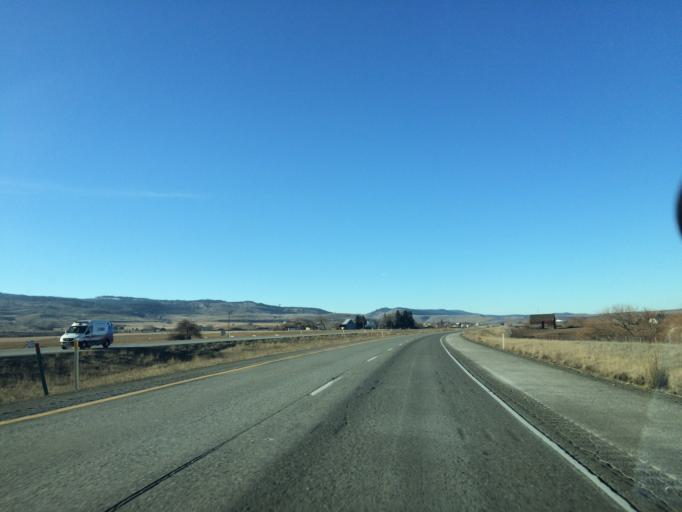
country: US
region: Washington
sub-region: Kittitas County
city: Ellensburg
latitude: 47.0625
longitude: -120.6899
